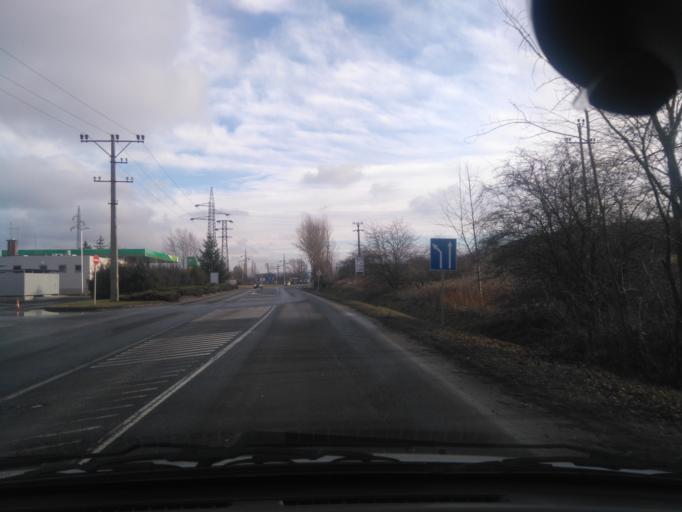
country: HU
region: Komarom-Esztergom
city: Dorog
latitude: 47.7244
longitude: 18.7189
